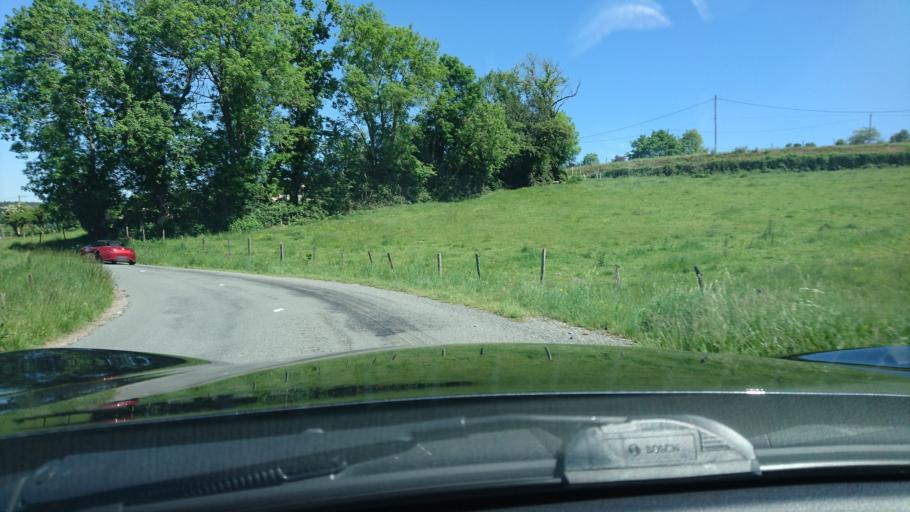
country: FR
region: Rhone-Alpes
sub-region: Departement de la Loire
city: Violay
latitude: 45.8871
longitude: 4.3324
